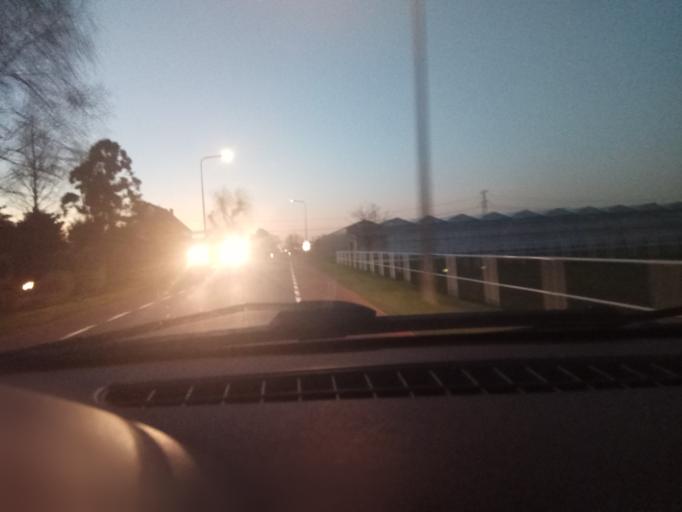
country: NL
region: South Holland
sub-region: Gemeente Westland
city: Maasdijk
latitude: 51.9644
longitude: 4.2023
